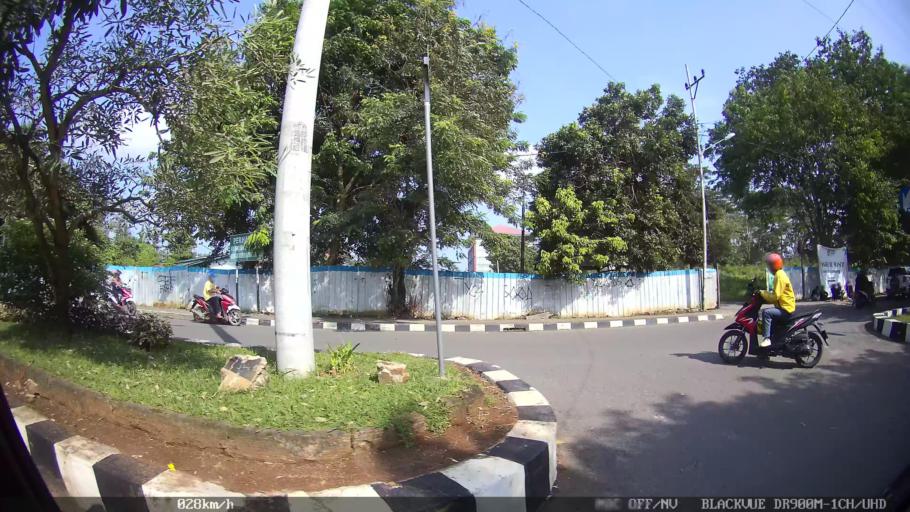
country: ID
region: Lampung
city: Kedaton
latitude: -5.3711
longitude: 105.2400
